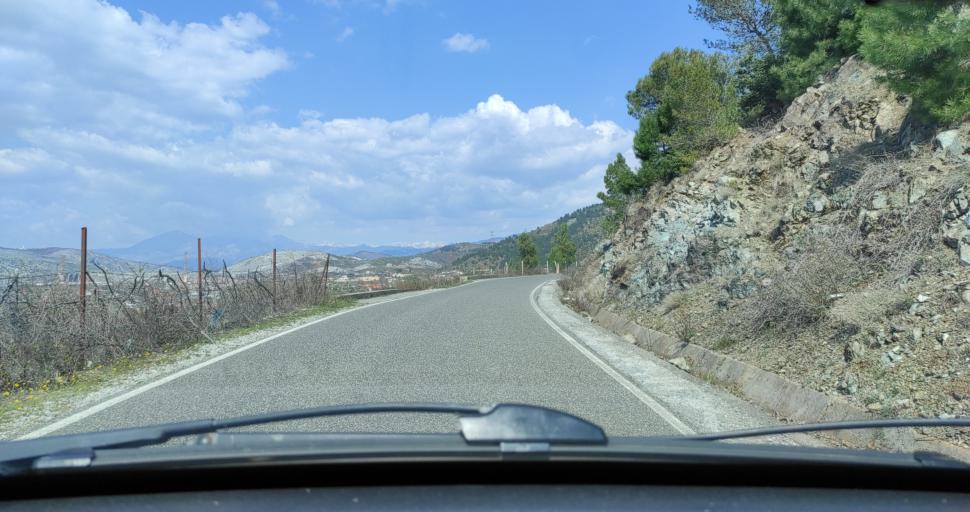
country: AL
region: Shkoder
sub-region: Rrethi i Shkodres
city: Vau i Dejes
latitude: 41.9904
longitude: 19.6444
